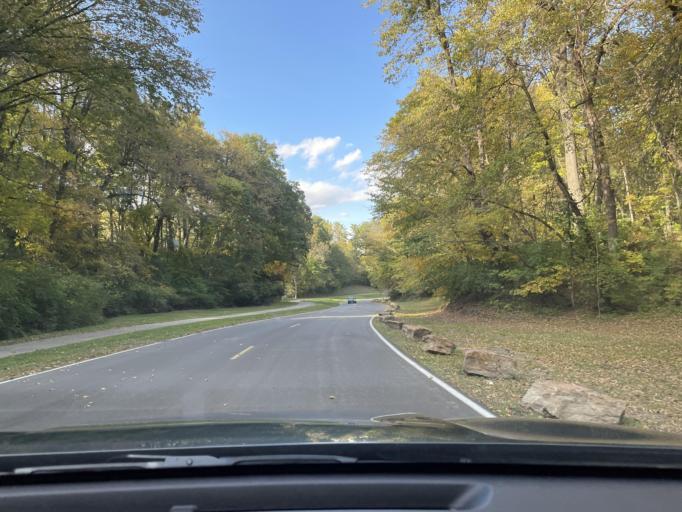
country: US
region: Kansas
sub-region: Doniphan County
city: Elwood
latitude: 39.7228
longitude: -94.8449
